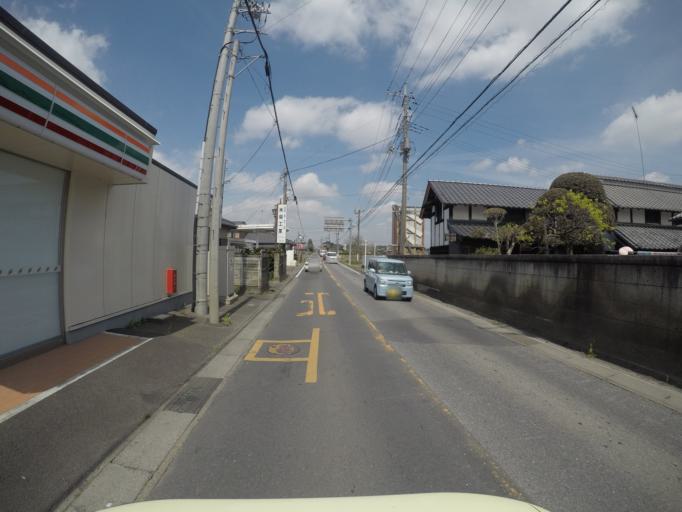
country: JP
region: Ibaraki
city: Makabe
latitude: 36.2514
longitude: 140.0360
